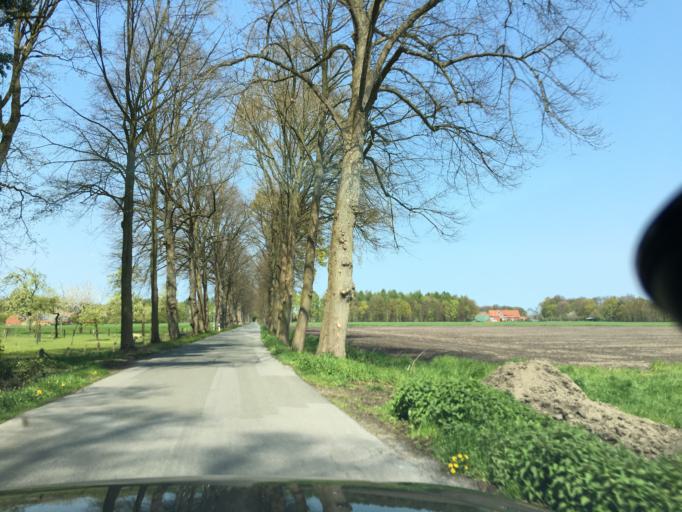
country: DE
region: North Rhine-Westphalia
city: Ludinghausen
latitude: 51.7891
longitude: 7.4328
